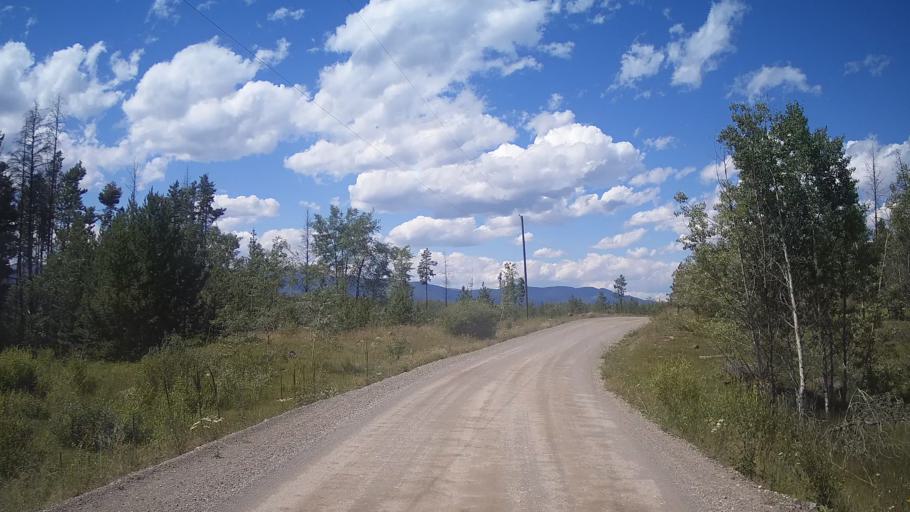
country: CA
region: British Columbia
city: Cache Creek
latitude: 51.2465
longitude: -121.6592
